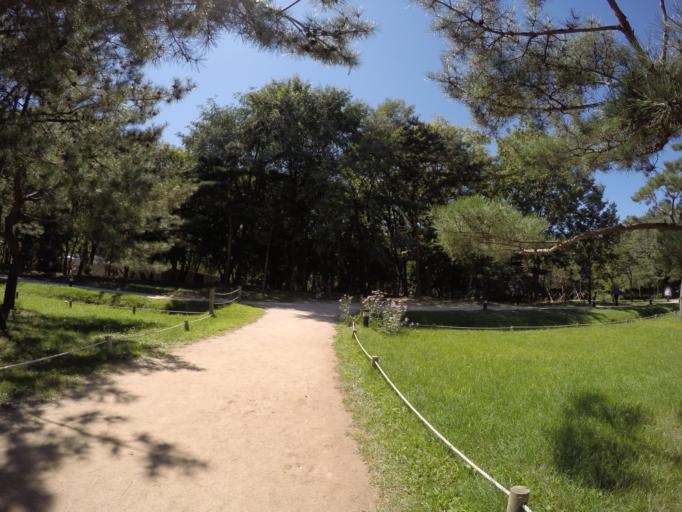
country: KR
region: Seoul
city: Seoul
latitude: 37.5082
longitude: 127.0524
